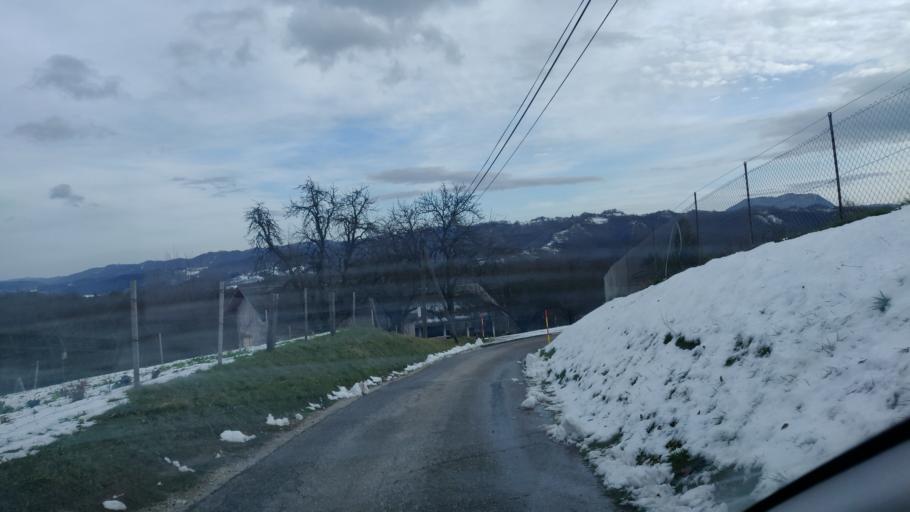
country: SI
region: Makole
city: Makole
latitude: 46.3300
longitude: 15.6553
